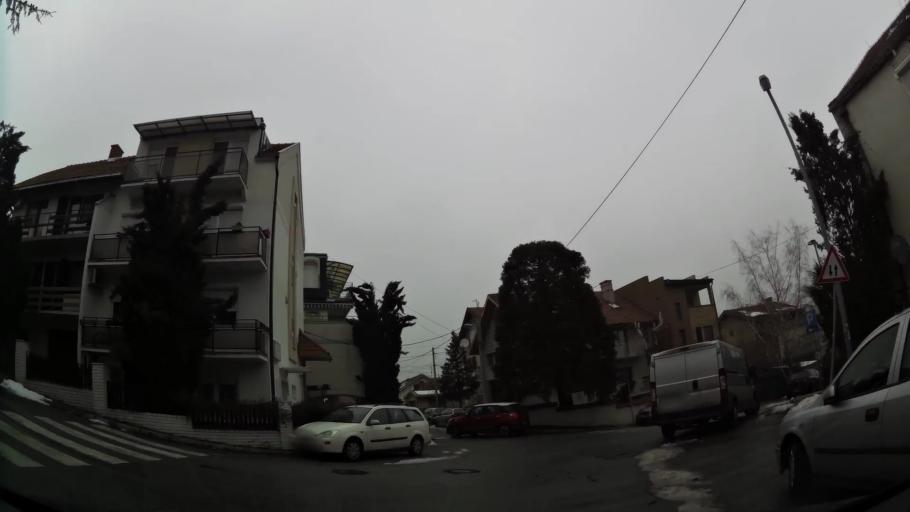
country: RS
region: Central Serbia
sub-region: Belgrade
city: Vozdovac
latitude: 44.7730
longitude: 20.4809
